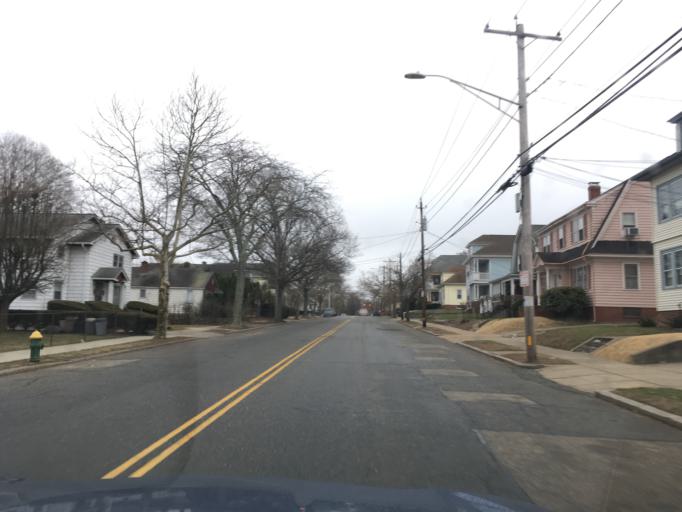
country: US
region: Rhode Island
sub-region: Providence County
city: North Providence
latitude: 41.8350
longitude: -71.4504
